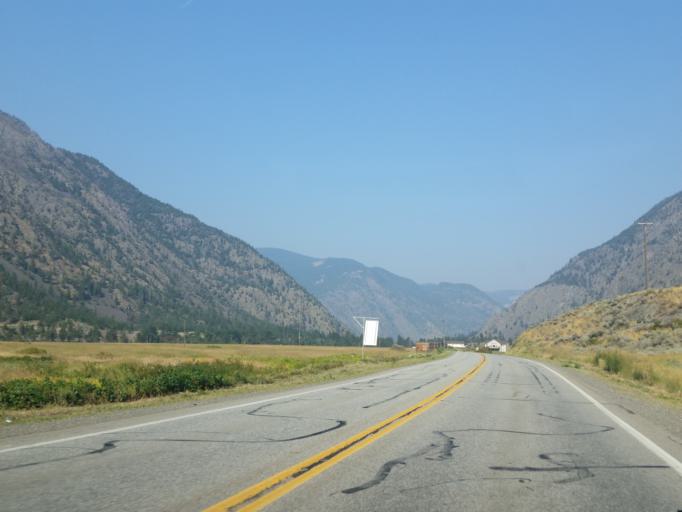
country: CA
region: British Columbia
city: Oliver
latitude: 49.2144
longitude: -119.9070
